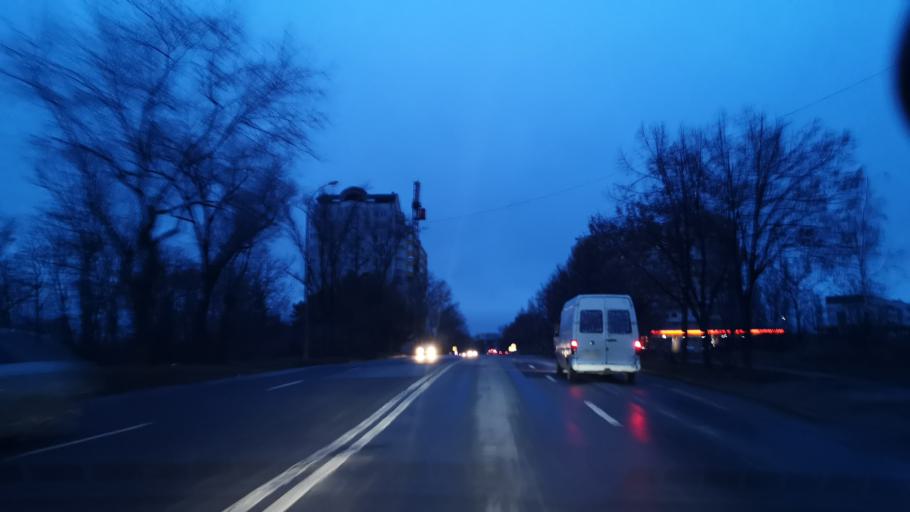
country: MD
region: Chisinau
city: Chisinau
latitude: 47.0306
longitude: 28.8792
